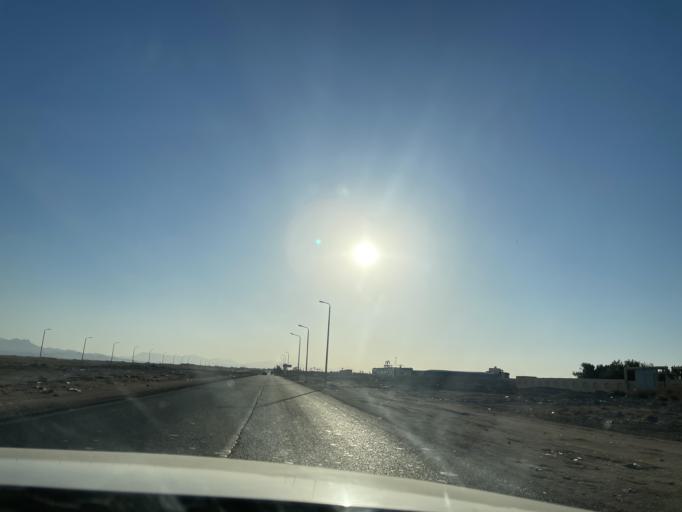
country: EG
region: Red Sea
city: Hurghada
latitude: 27.2170
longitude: 33.8025
